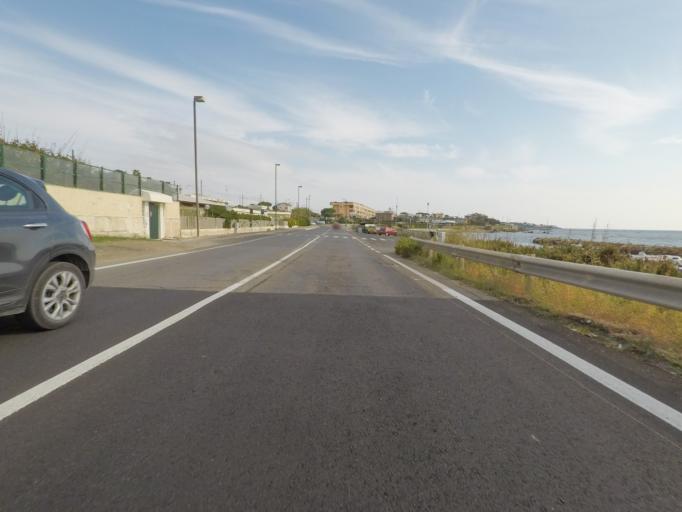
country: IT
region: Latium
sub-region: Citta metropolitana di Roma Capitale
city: Santa Marinella
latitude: 42.0453
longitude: 11.8255
